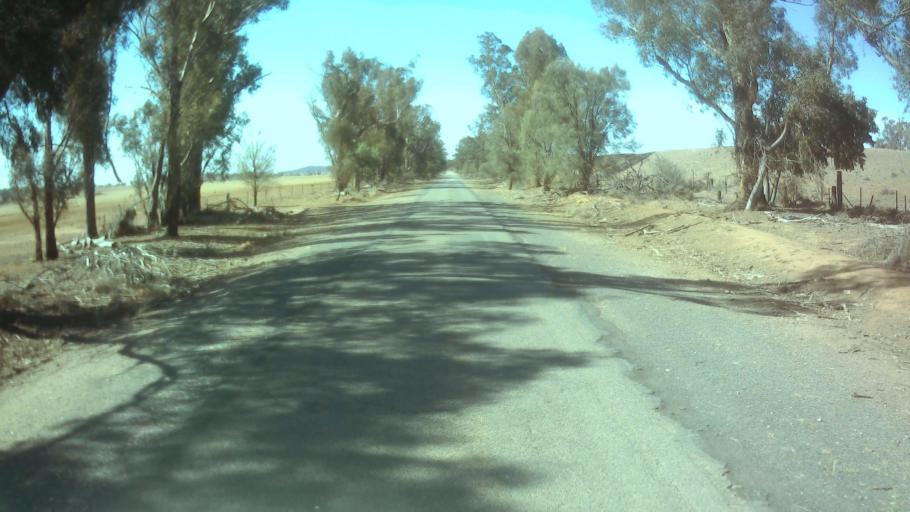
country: AU
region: New South Wales
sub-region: Forbes
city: Forbes
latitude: -33.7237
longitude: 147.7448
